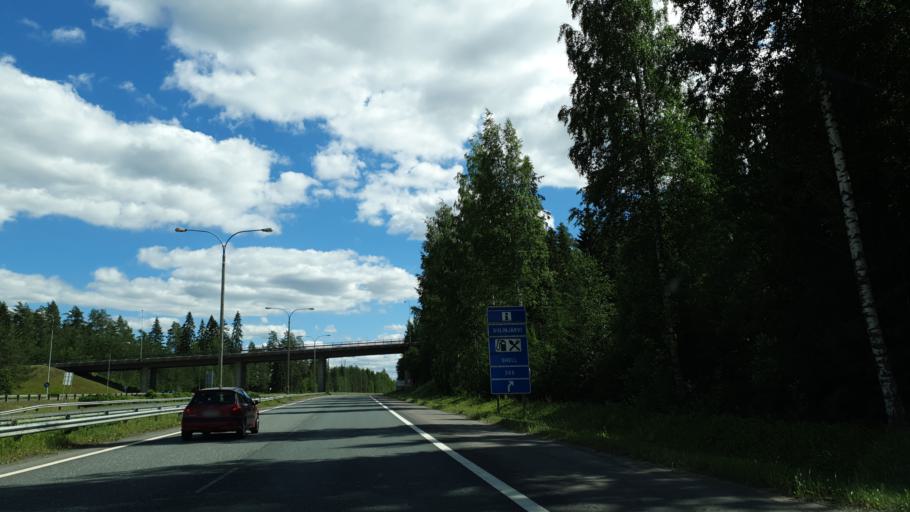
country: FI
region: Northern Savo
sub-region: Kuopio
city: Siilinjaervi
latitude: 63.0702
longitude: 27.6594
